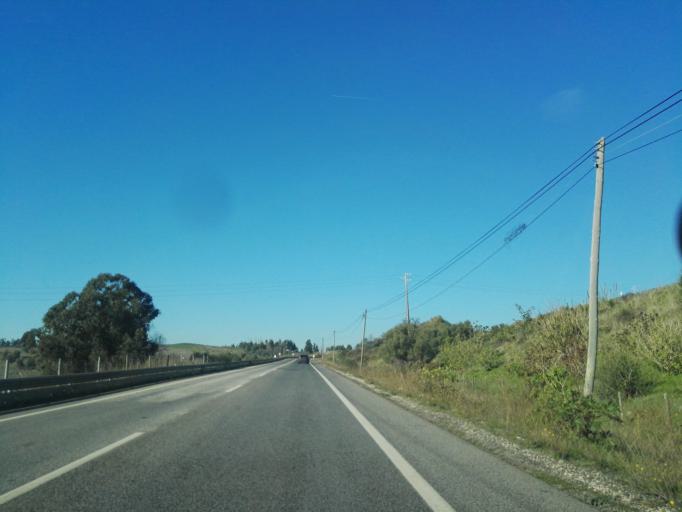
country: PT
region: Lisbon
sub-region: Loures
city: Loures
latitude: 38.8530
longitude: -9.1823
